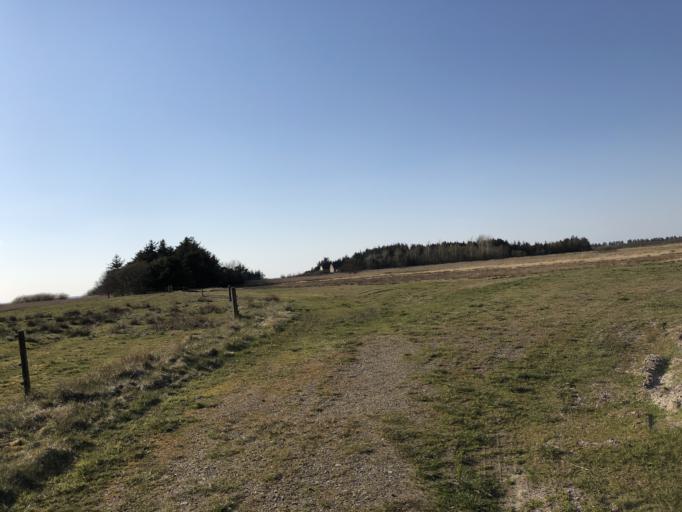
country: DK
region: Central Jutland
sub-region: Holstebro Kommune
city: Ulfborg
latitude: 56.3491
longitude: 8.2516
